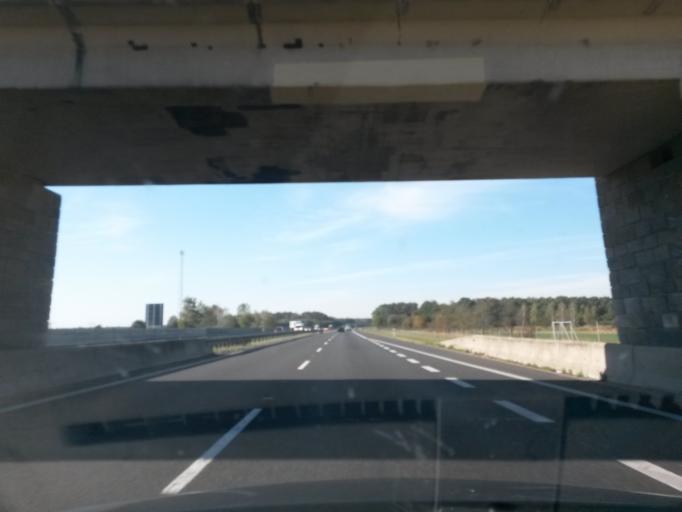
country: PL
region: Opole Voivodeship
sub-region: Powiat opolski
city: Niemodlin
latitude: 50.6792
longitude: 17.6498
